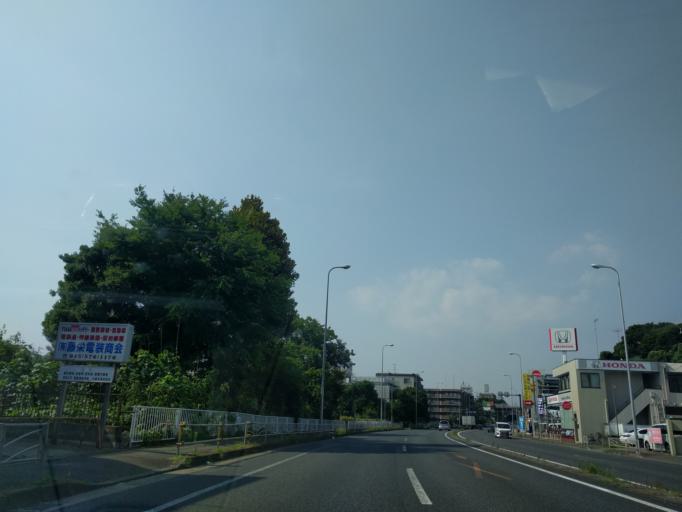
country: JP
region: Kanagawa
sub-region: Kawasaki-shi
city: Kawasaki
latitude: 35.5072
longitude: 139.6618
